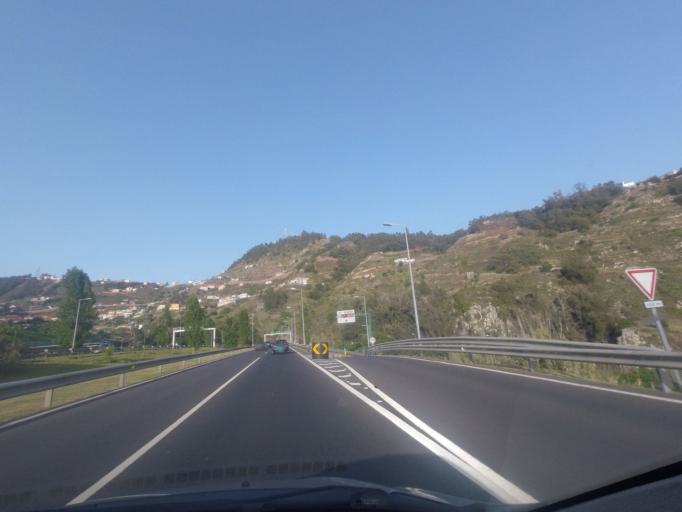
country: PT
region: Madeira
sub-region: Ribeira Brava
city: Campanario
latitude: 32.6585
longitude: -17.0144
